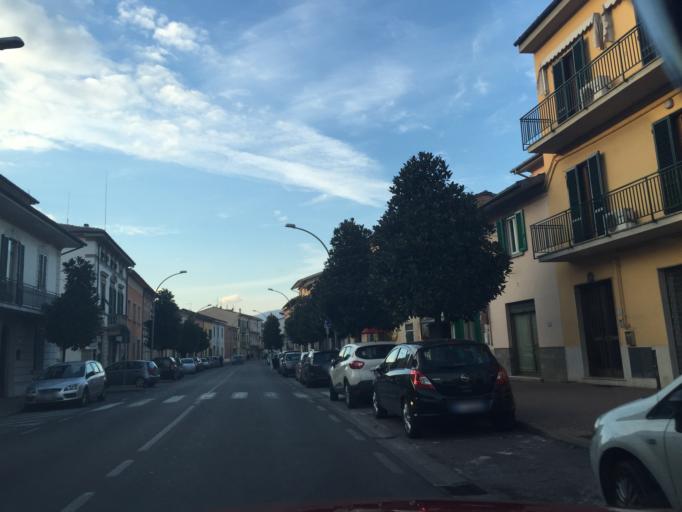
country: IT
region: Tuscany
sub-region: Provincia di Pistoia
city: Monsummano Terme
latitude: 43.8669
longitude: 10.8167
